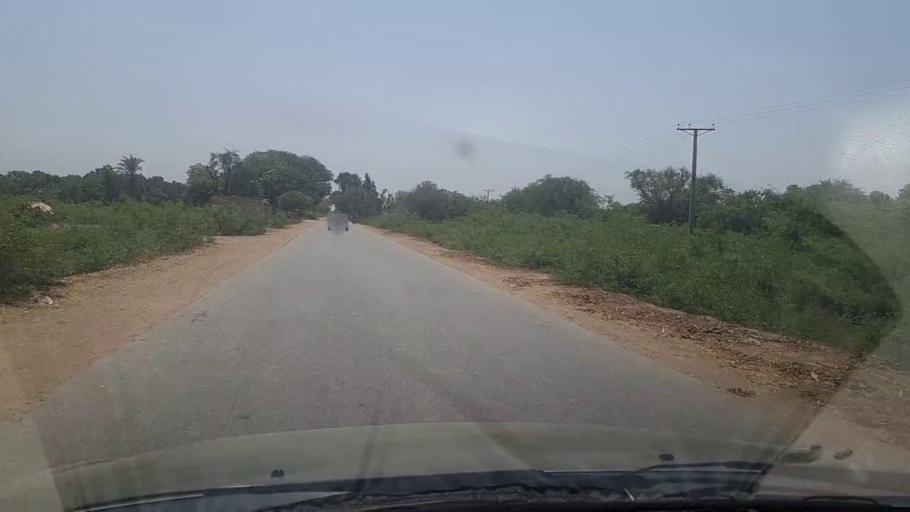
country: PK
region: Sindh
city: Tando Jam
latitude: 25.3047
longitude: 68.5800
